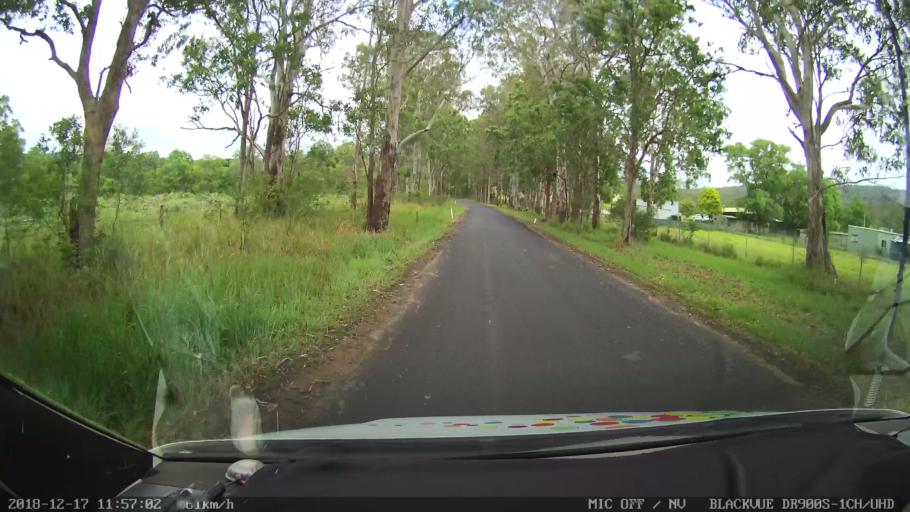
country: AU
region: New South Wales
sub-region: Kyogle
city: Kyogle
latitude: -28.5428
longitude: 152.5767
